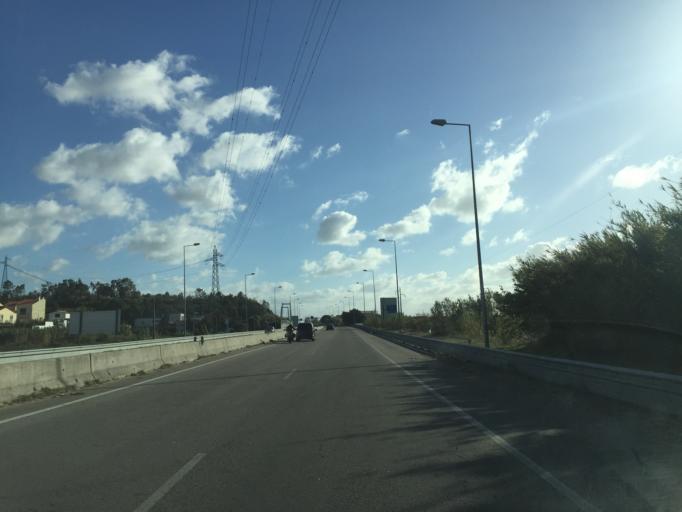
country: PT
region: Coimbra
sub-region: Figueira da Foz
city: Tavarede
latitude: 40.1588
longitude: -8.8409
